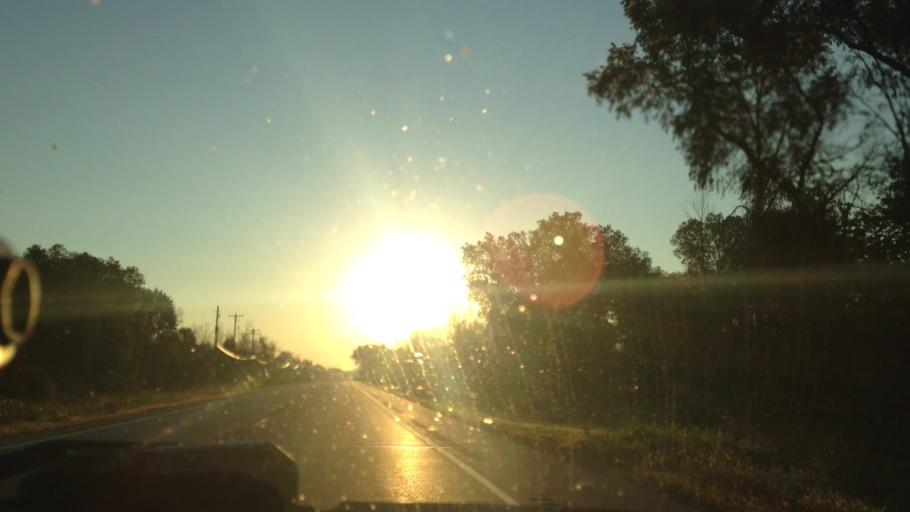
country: US
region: Wisconsin
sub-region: Washington County
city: Newburg
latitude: 43.4249
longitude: -88.1130
